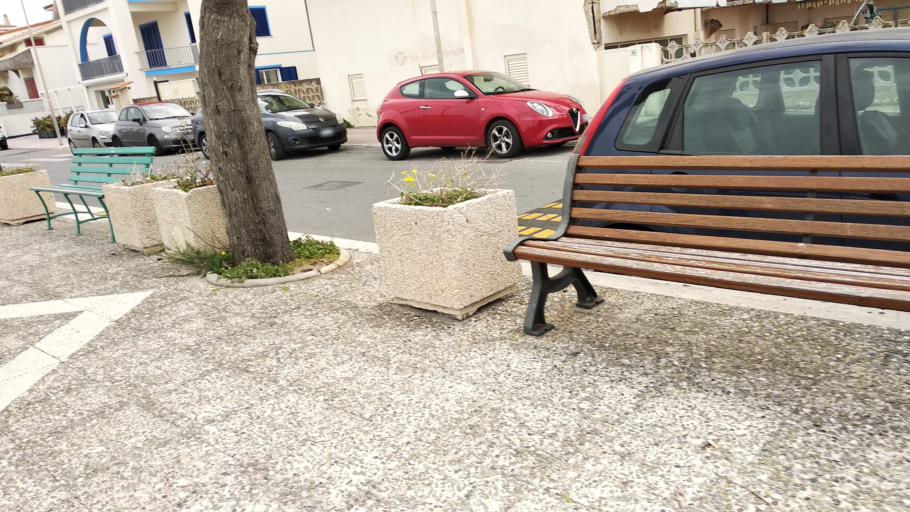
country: IT
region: Sicily
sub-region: Messina
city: Venetico Marina
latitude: 38.2213
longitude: 15.3674
